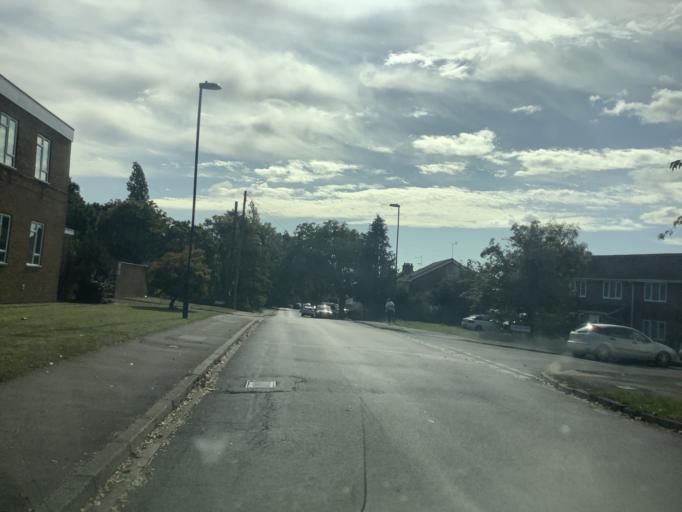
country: GB
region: England
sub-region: Hampshire
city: Marchwood
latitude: 50.9260
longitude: -1.4486
